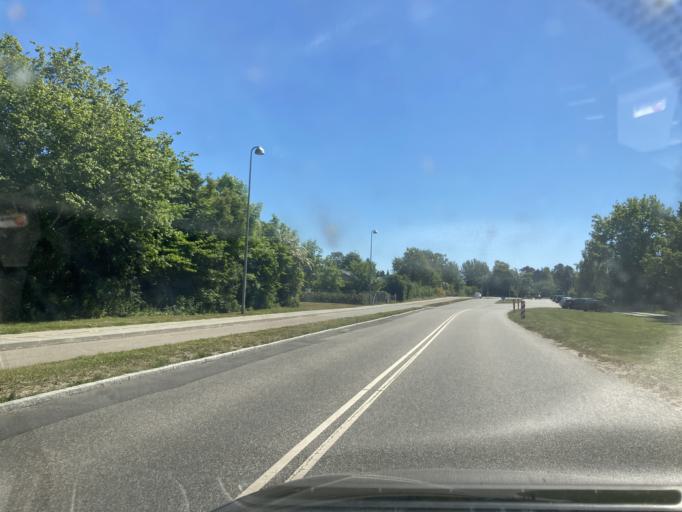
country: DK
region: Zealand
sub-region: Greve Kommune
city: Greve
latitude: 55.5812
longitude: 12.3011
